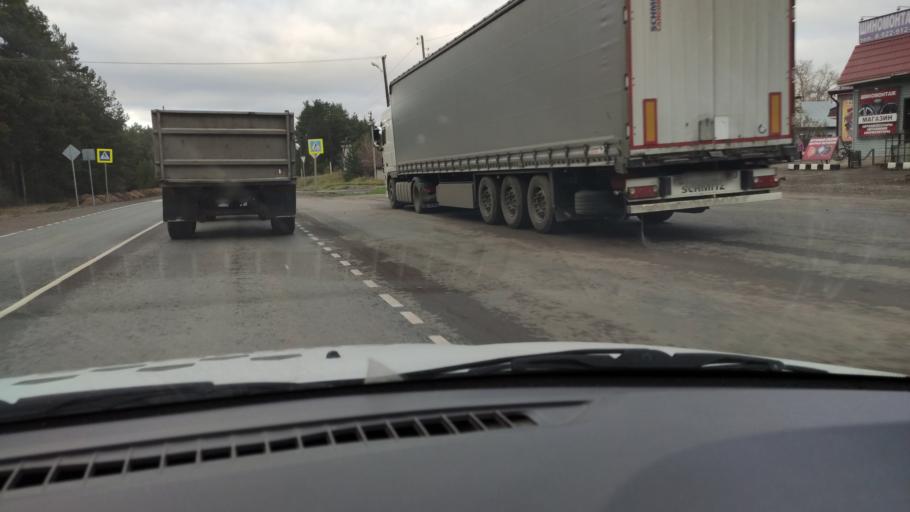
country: RU
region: Kirov
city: Belaya Kholunitsa
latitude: 58.8497
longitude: 50.8279
